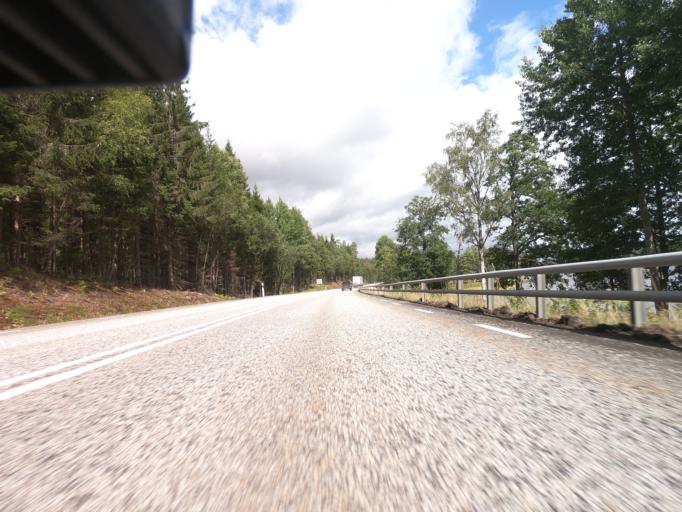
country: SE
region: Joenkoeping
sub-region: Vaggeryds Kommun
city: Vaggeryd
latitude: 57.5446
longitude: 14.2643
